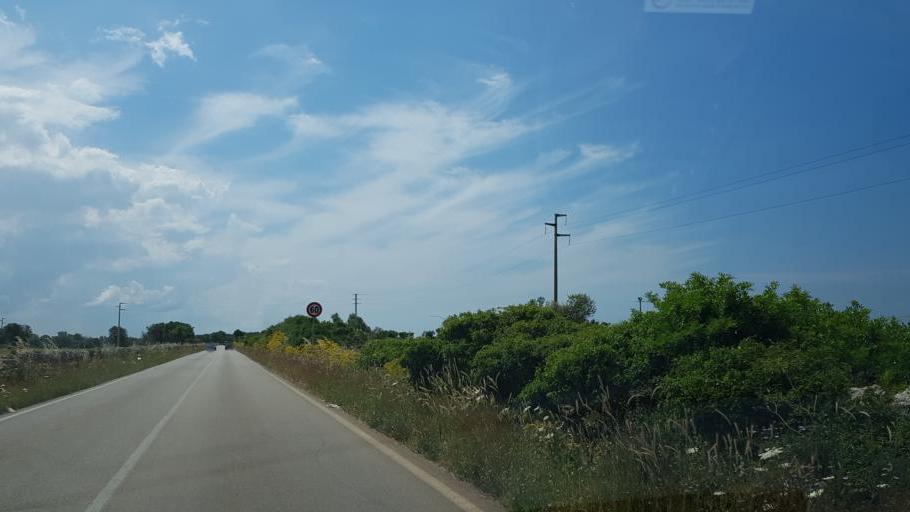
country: IT
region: Apulia
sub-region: Provincia di Lecce
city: Porto Cesareo
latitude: 40.3201
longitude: 17.8582
